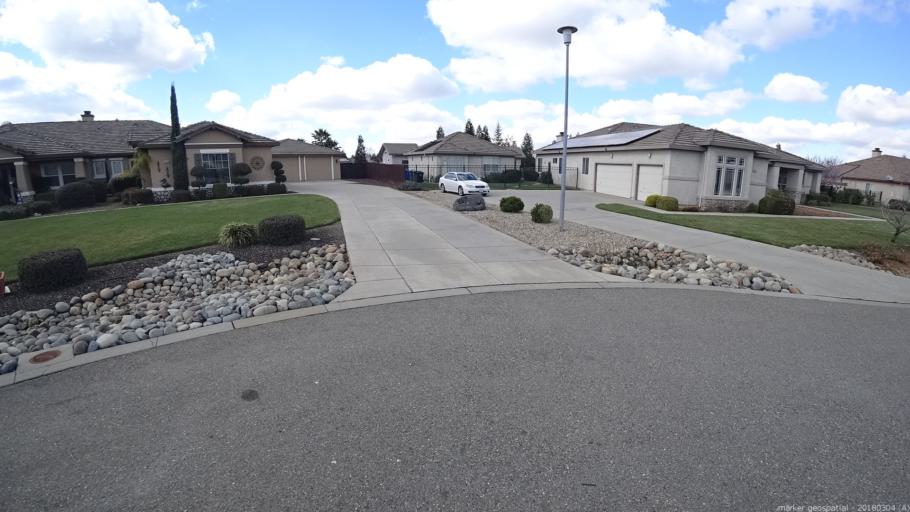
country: US
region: California
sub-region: Sacramento County
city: Vineyard
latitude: 38.4587
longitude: -121.3001
